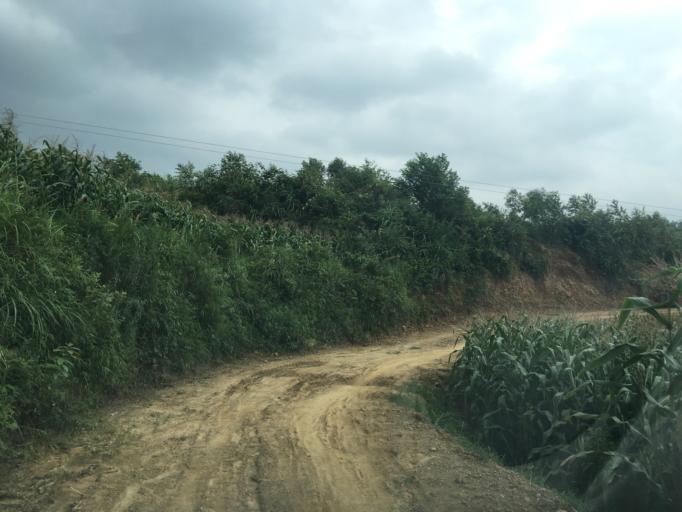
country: CN
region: Guangxi Zhuangzu Zizhiqu
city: Xinzhou
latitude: 25.1625
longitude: 105.6846
